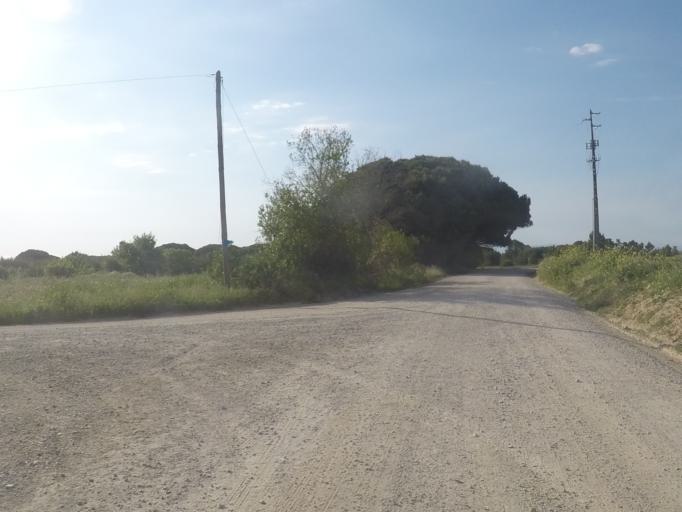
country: PT
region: Setubal
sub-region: Sesimbra
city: Sesimbra
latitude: 38.4431
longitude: -9.1968
